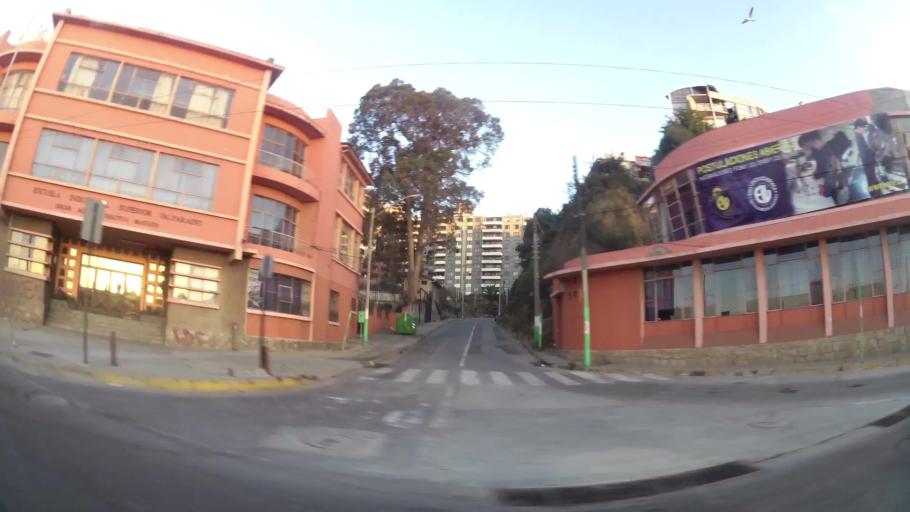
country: CL
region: Valparaiso
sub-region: Provincia de Valparaiso
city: Vina del Mar
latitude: -33.0287
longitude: -71.5863
